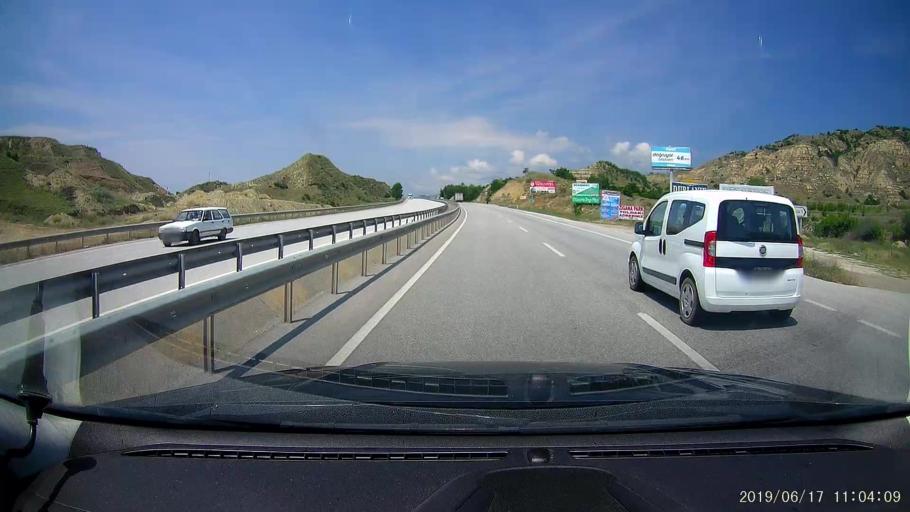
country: TR
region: Kastamonu
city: Tosya
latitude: 41.0207
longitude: 34.1012
